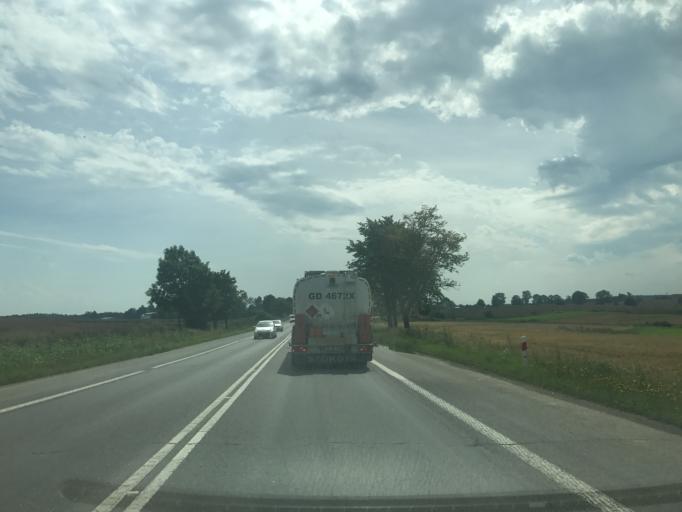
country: PL
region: Warmian-Masurian Voivodeship
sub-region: Powiat ostrodzki
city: Ostroda
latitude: 53.6537
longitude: 20.0517
